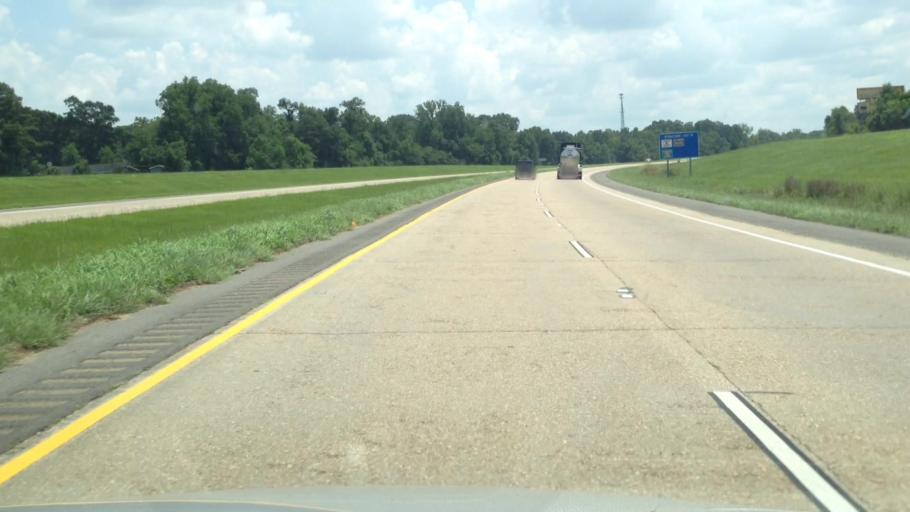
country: US
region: Louisiana
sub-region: Saint Landry Parish
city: Opelousas
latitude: 30.5477
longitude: -92.0537
